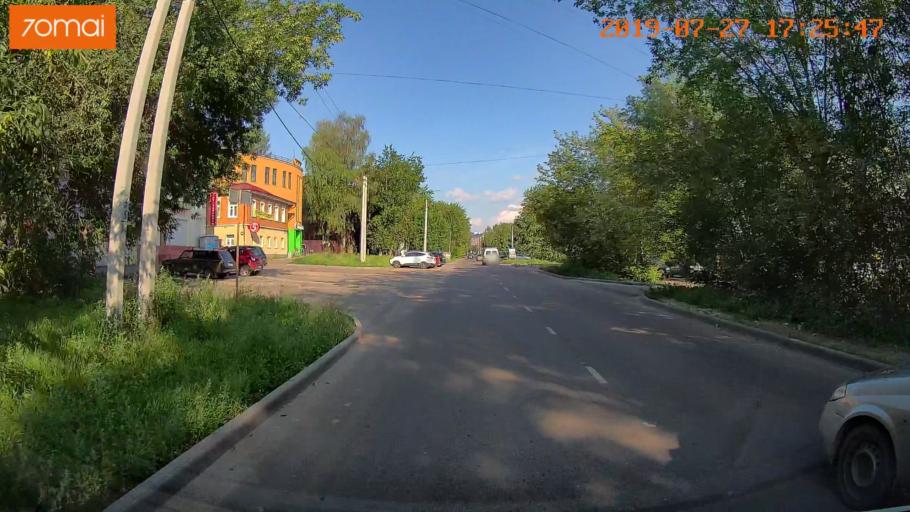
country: RU
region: Ivanovo
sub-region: Gorod Ivanovo
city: Ivanovo
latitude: 57.0162
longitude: 40.9638
